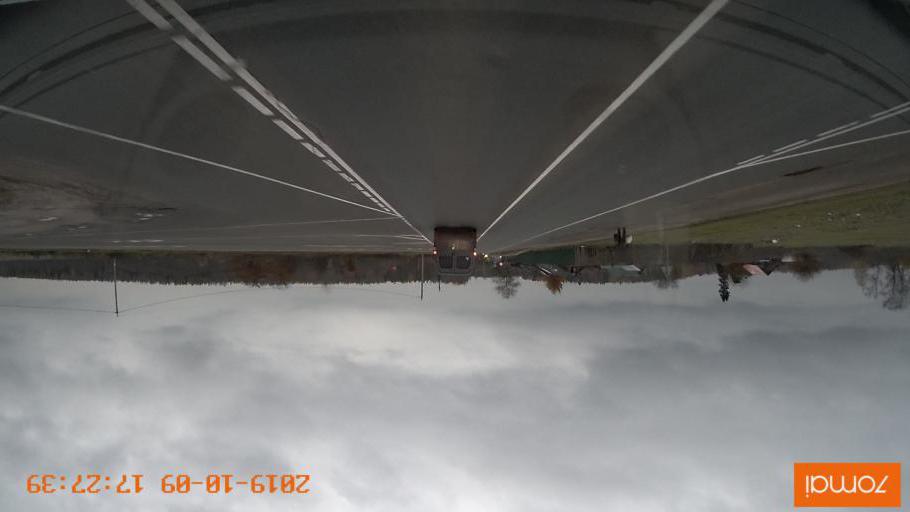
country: RU
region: Ivanovo
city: Furmanov
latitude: 57.1648
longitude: 41.0702
